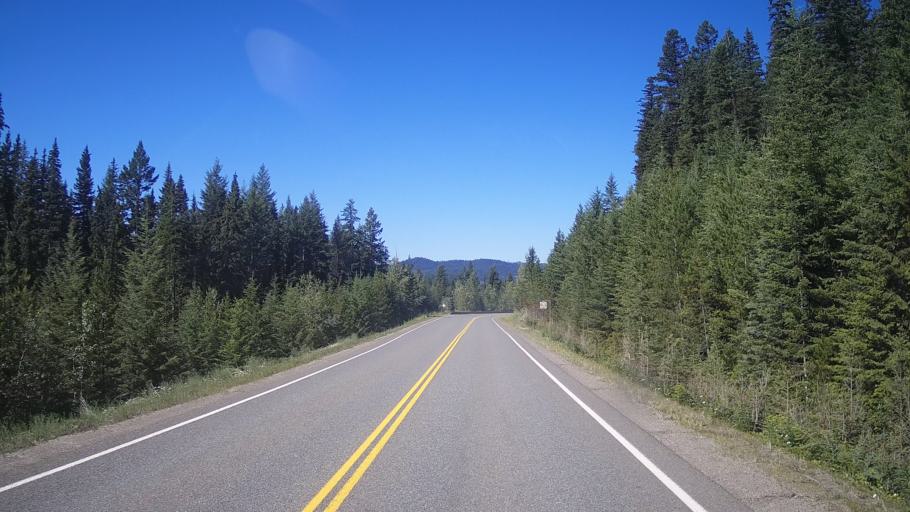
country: CA
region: British Columbia
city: Kamloops
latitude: 51.4776
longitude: -120.4728
